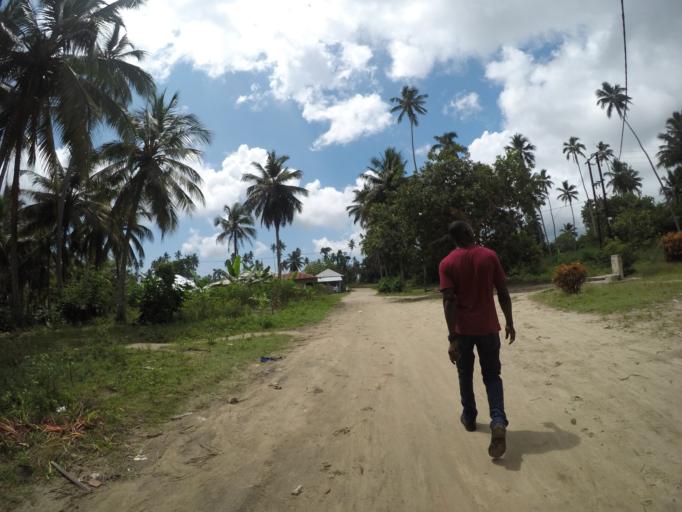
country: TZ
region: Pemba South
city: Mtambile
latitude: -5.3852
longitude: 39.7429
